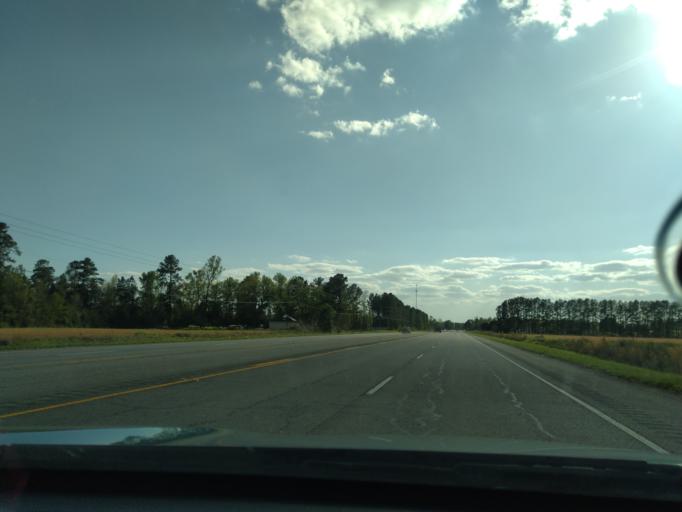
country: US
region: South Carolina
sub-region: Williamsburg County
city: Kingstree
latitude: 33.6468
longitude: -79.8906
